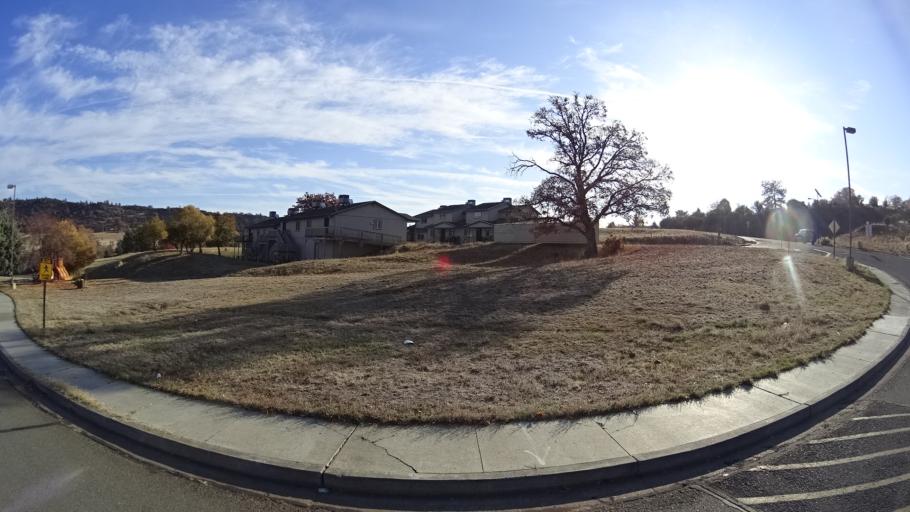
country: US
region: California
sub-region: Siskiyou County
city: Yreka
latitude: 41.7113
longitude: -122.6261
